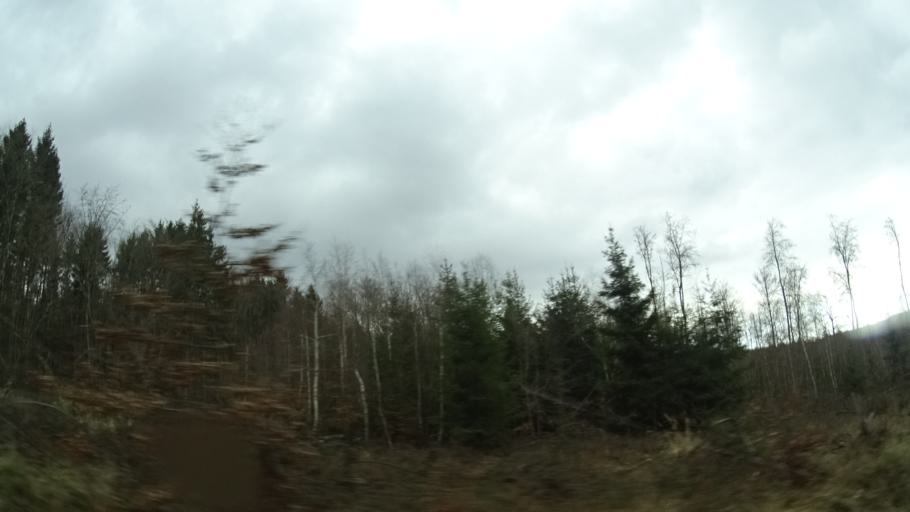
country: DE
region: Rheinland-Pfalz
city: Daxweiler
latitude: 49.9884
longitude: 7.7692
